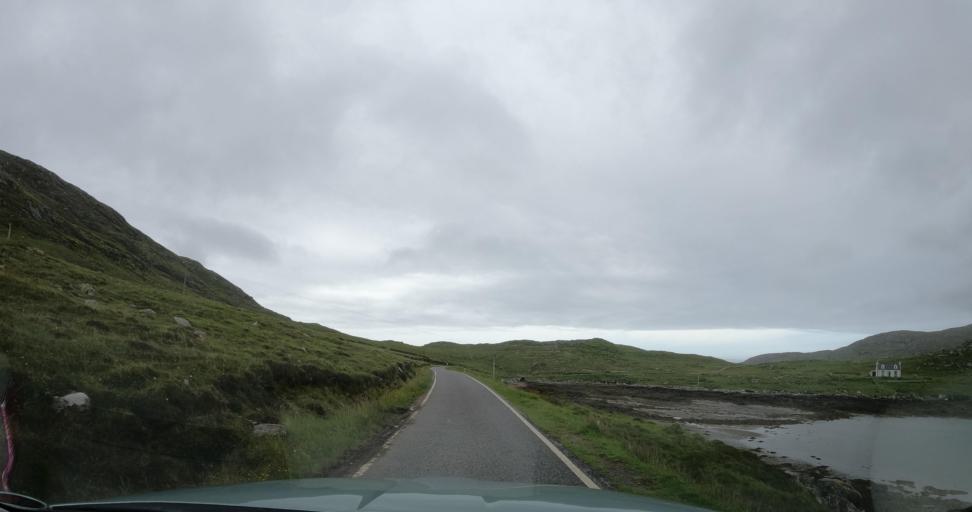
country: GB
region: Scotland
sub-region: Eilean Siar
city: Barra
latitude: 56.9386
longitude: -7.5396
